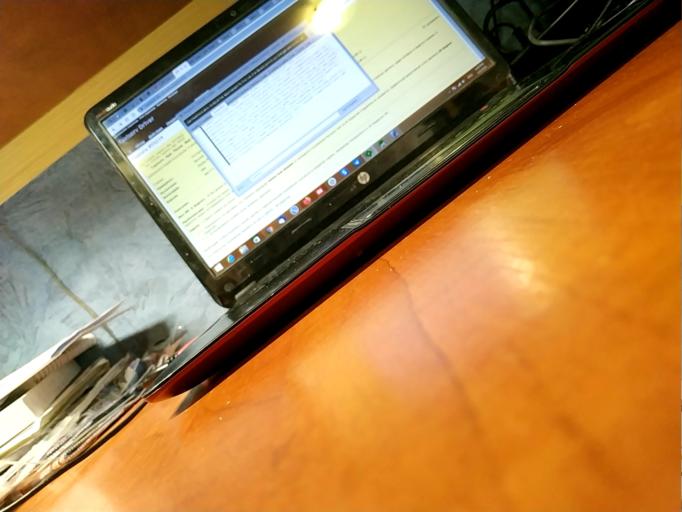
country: RU
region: Tverskaya
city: Sandovo
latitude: 58.4682
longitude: 36.3987
